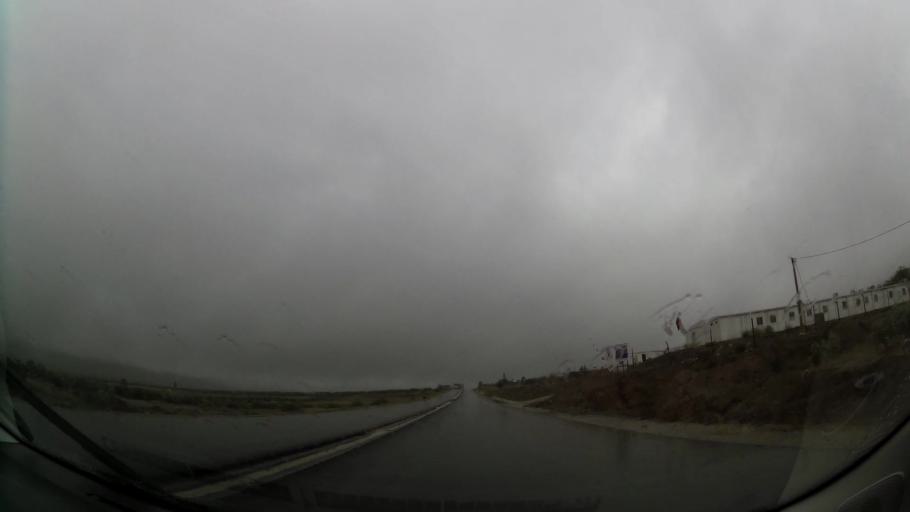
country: MA
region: Oriental
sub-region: Nador
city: Midar
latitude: 34.8646
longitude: -3.7242
